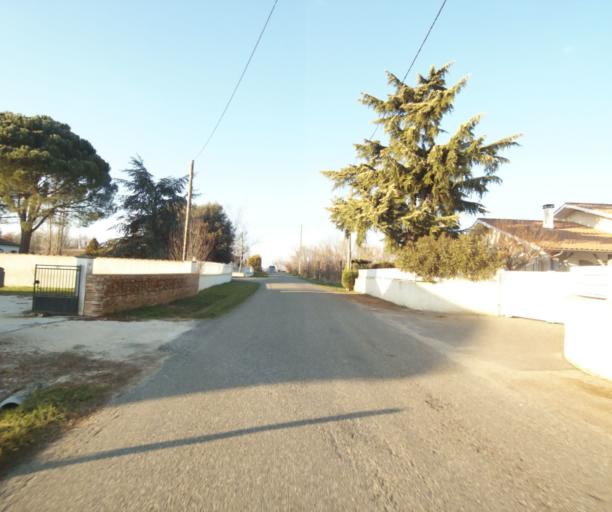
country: FR
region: Midi-Pyrenees
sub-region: Departement du Tarn-et-Garonne
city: Moissac
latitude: 44.1272
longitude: 1.1229
